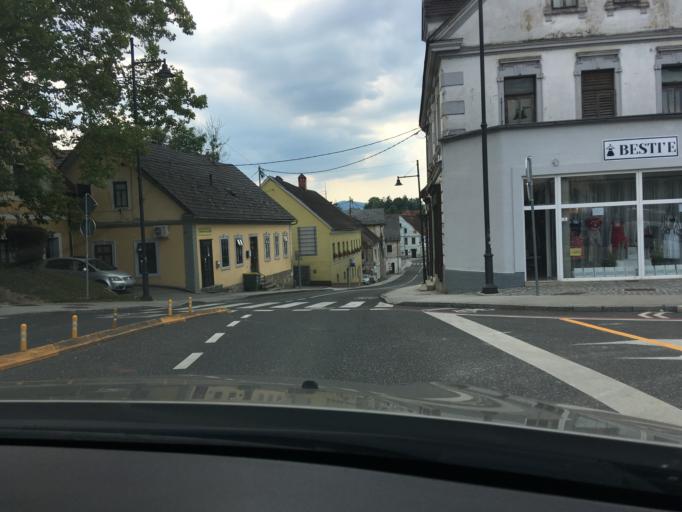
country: SI
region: Novo Mesto
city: Novo Mesto
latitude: 45.8011
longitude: 15.1711
